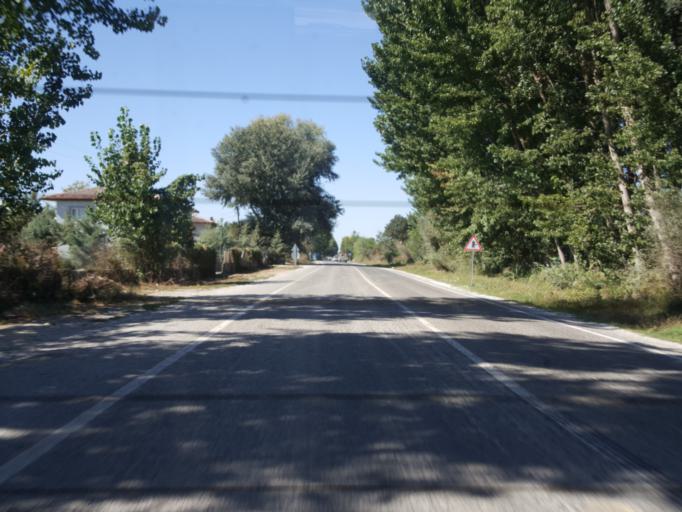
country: TR
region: Tokat
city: Pazar
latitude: 40.2703
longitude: 36.2472
